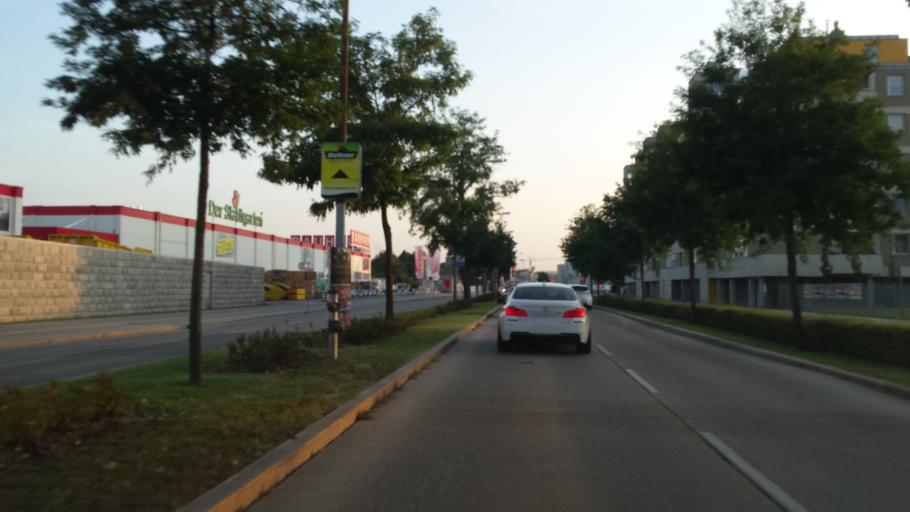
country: AT
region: Lower Austria
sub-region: Politischer Bezirk Wien-Umgebung
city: Gerasdorf bei Wien
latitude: 48.2552
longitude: 16.4475
